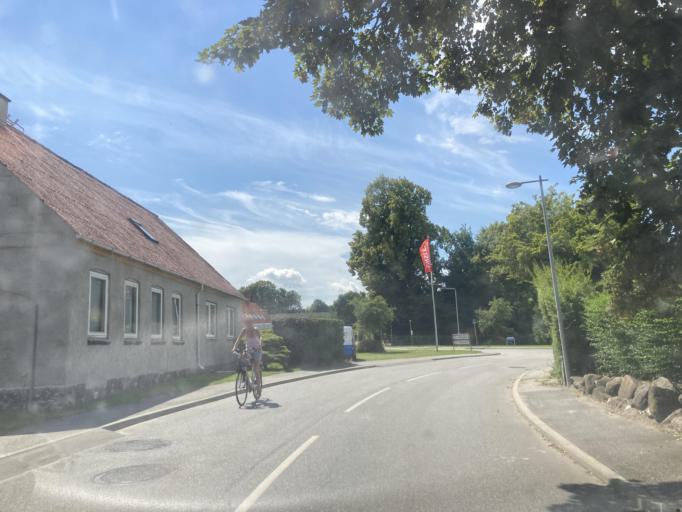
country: DK
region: Zealand
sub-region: Faxe Kommune
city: Haslev
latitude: 55.3867
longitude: 11.9383
